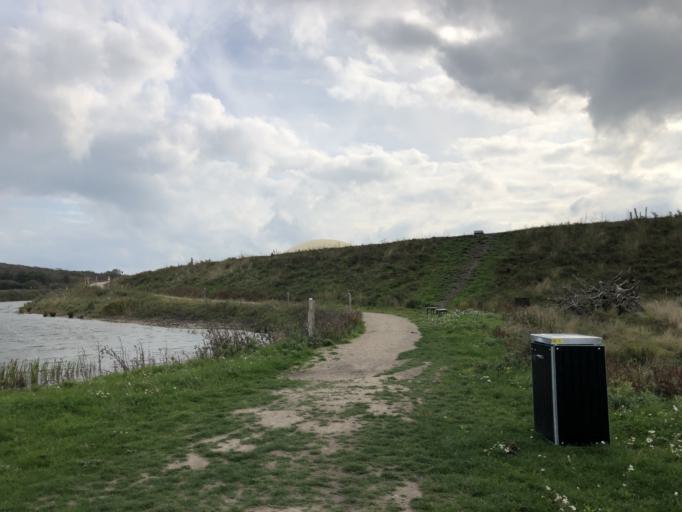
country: DK
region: Central Jutland
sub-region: Ringkobing-Skjern Kommune
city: Ringkobing
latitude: 56.1025
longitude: 8.2410
